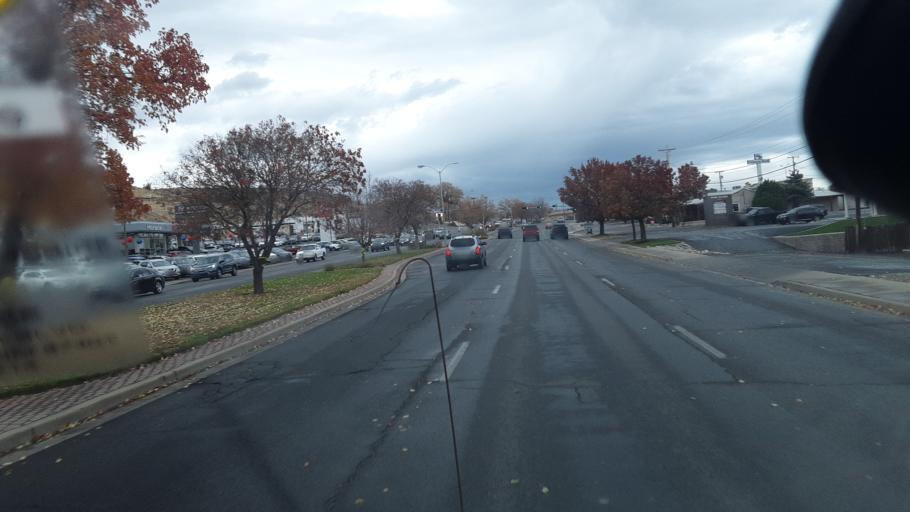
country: US
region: New Mexico
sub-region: San Juan County
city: Farmington
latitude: 36.7595
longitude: -108.1558
